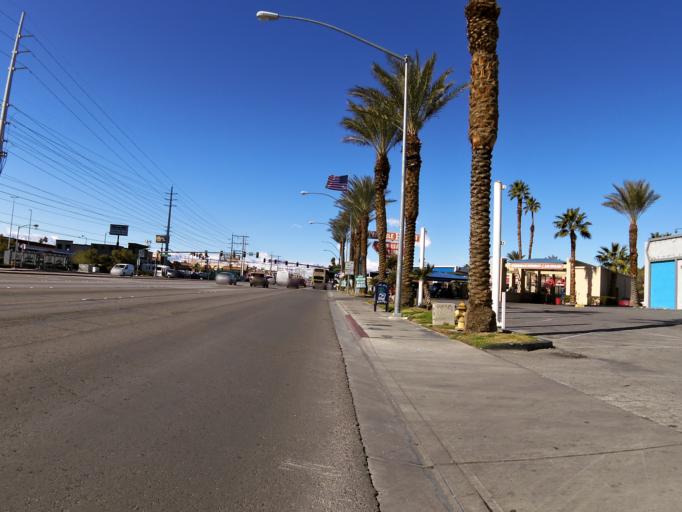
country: US
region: Nevada
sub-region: Clark County
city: Spring Valley
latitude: 36.1157
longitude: -115.1979
